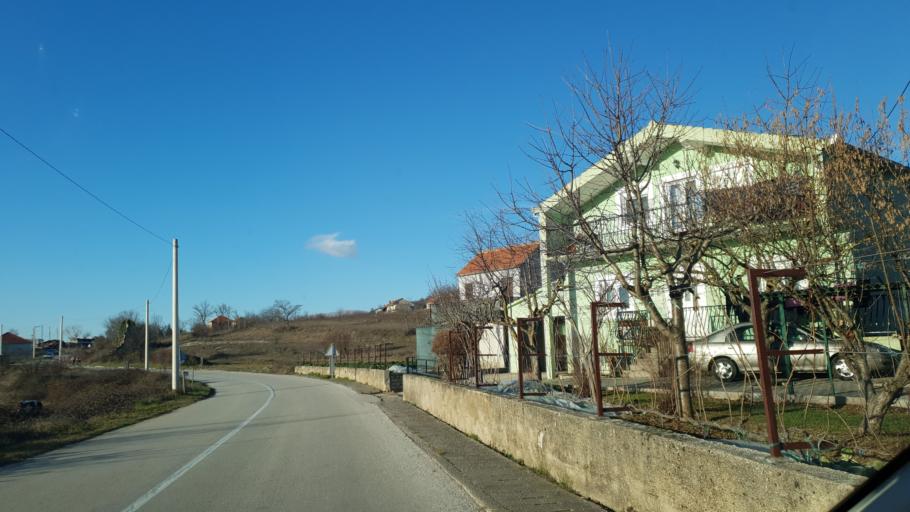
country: HR
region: Splitsko-Dalmatinska
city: Gala
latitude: 43.7351
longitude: 16.6856
